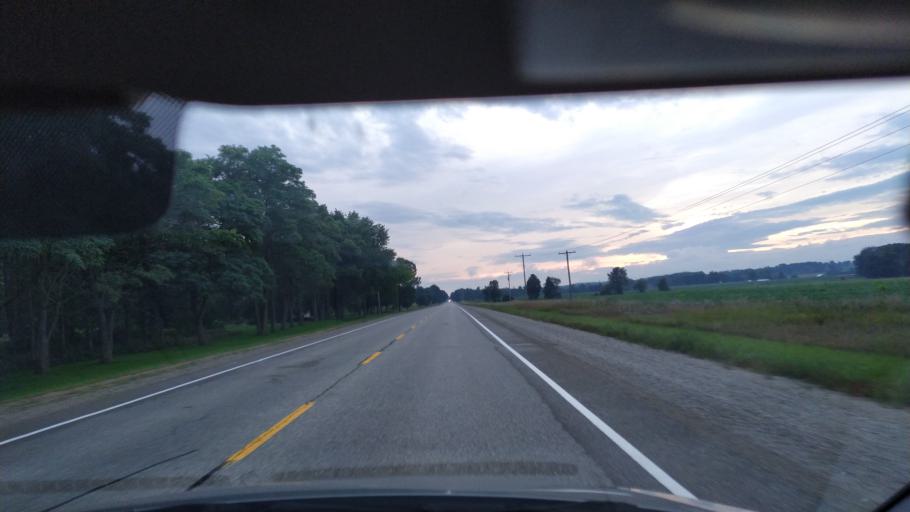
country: CA
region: Ontario
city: Kitchener
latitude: 43.3188
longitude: -80.5237
